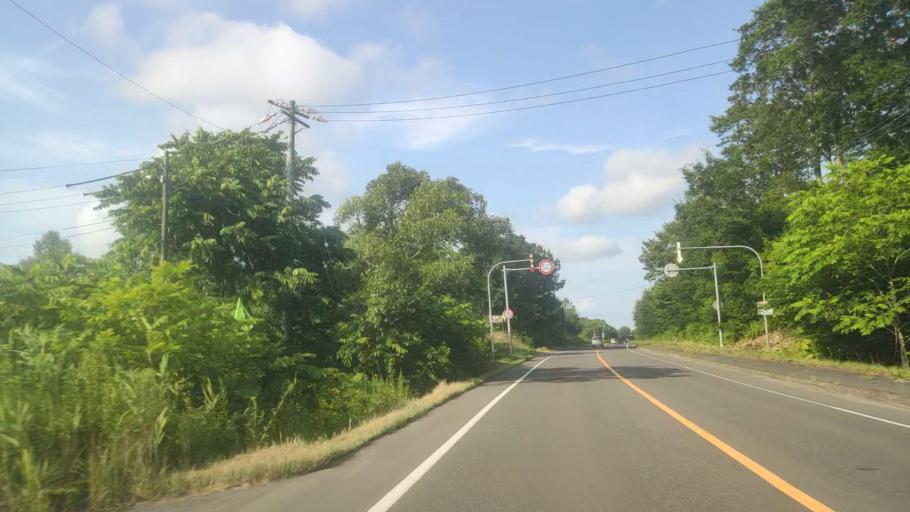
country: JP
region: Hokkaido
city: Chitose
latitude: 42.7345
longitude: 141.7769
